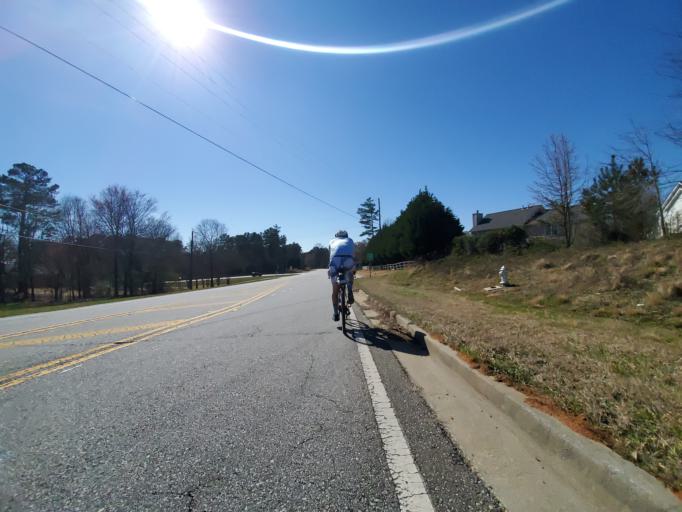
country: US
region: Georgia
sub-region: Gwinnett County
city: Dacula
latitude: 33.9650
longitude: -83.9112
